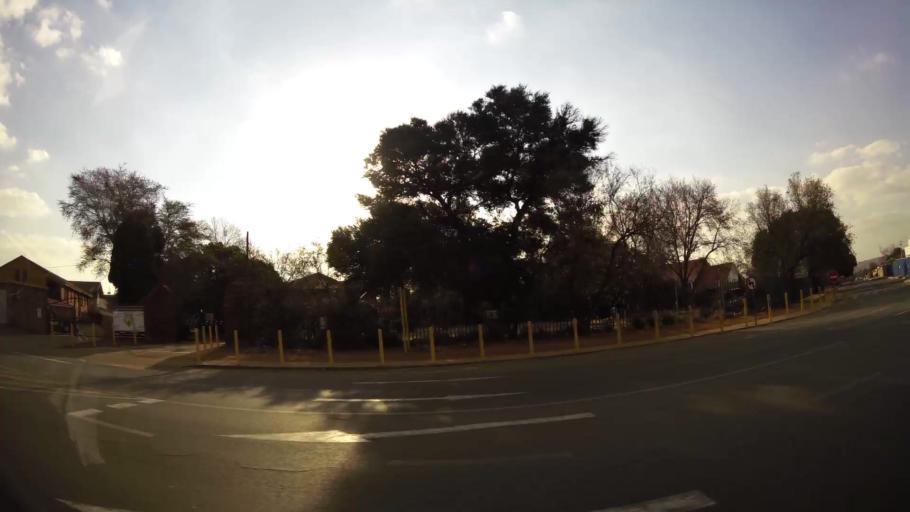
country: ZA
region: Gauteng
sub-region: West Rand District Municipality
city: Krugersdorp
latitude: -26.0985
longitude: 27.7427
